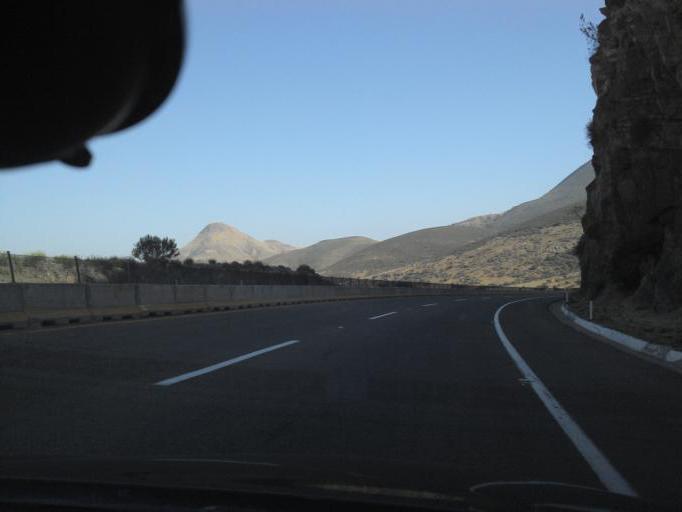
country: MX
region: Baja California
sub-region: Tijuana
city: El Nino
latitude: 32.5553
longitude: -116.8052
